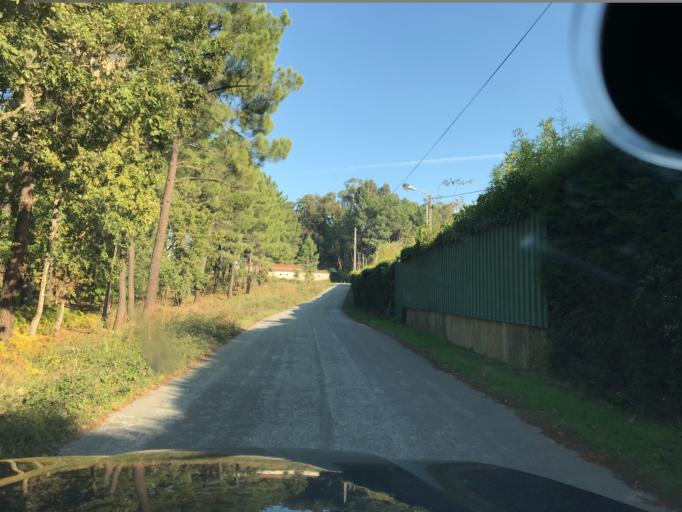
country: PT
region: Vila Real
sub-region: Vila Real
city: Vila Real
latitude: 41.3178
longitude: -7.7519
